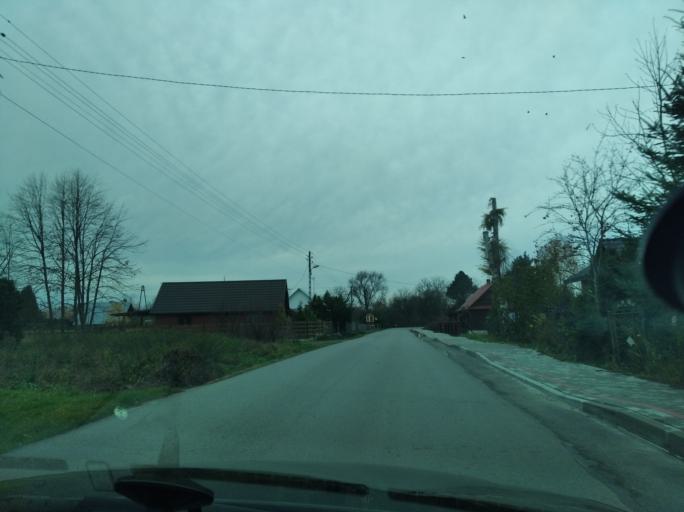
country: PL
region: Subcarpathian Voivodeship
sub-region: Powiat przeworski
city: Grzeska
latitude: 50.0842
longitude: 22.4490
